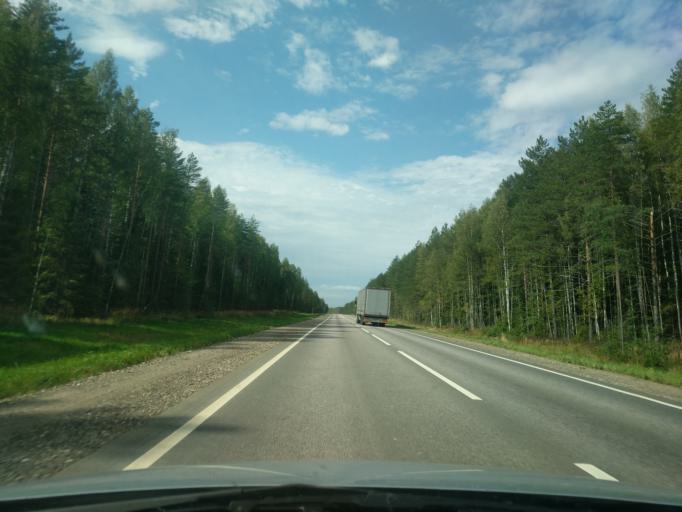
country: RU
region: Kostroma
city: Kadyy
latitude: 57.7986
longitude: 42.8296
